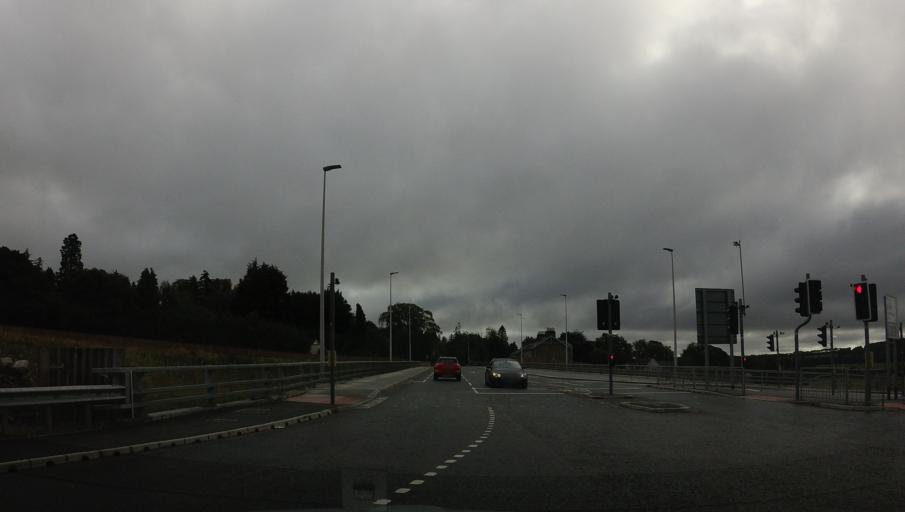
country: GB
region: Scotland
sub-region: Aberdeenshire
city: Westhill
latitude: 57.1017
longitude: -2.2446
